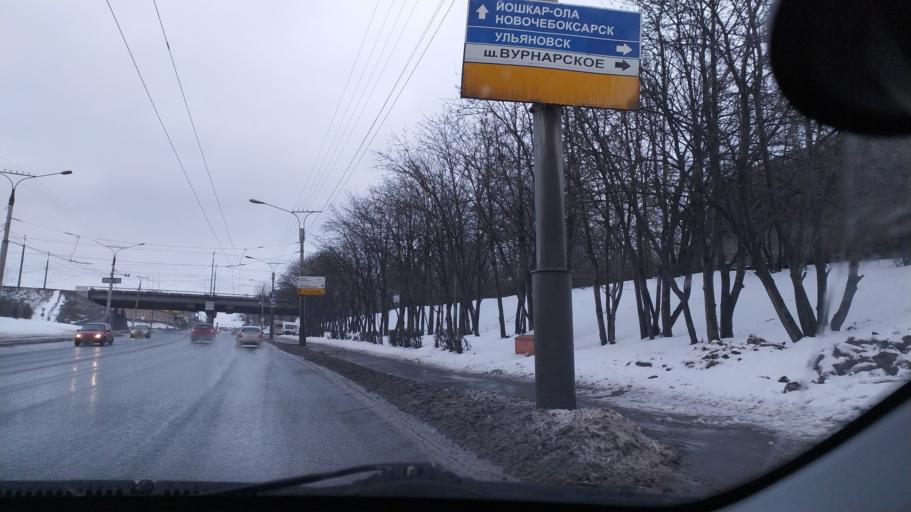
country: RU
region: Chuvashia
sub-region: Cheboksarskiy Rayon
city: Cheboksary
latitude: 56.1211
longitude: 47.2446
